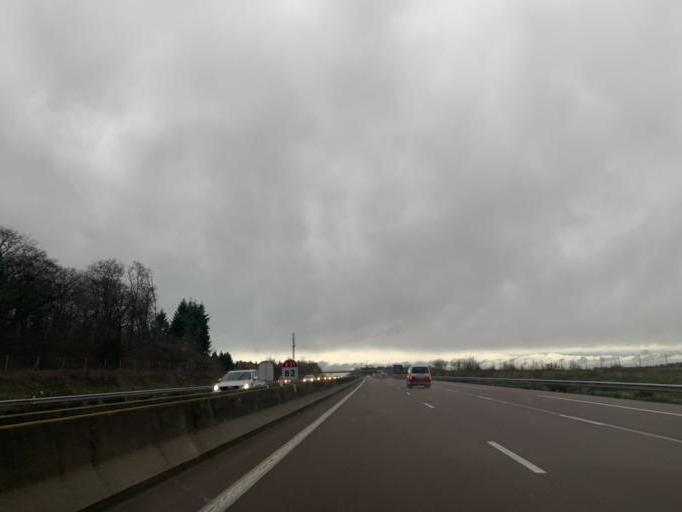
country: FR
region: Bourgogne
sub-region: Departement de la Cote-d'Or
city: Selongey
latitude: 47.6385
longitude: 5.1803
